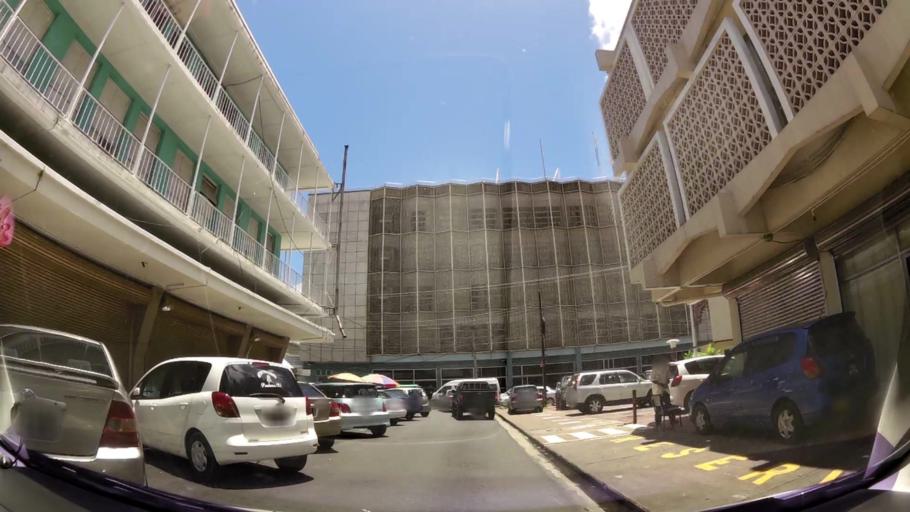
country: GY
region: Demerara-Mahaica
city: Georgetown
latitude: 6.8128
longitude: -58.1655
